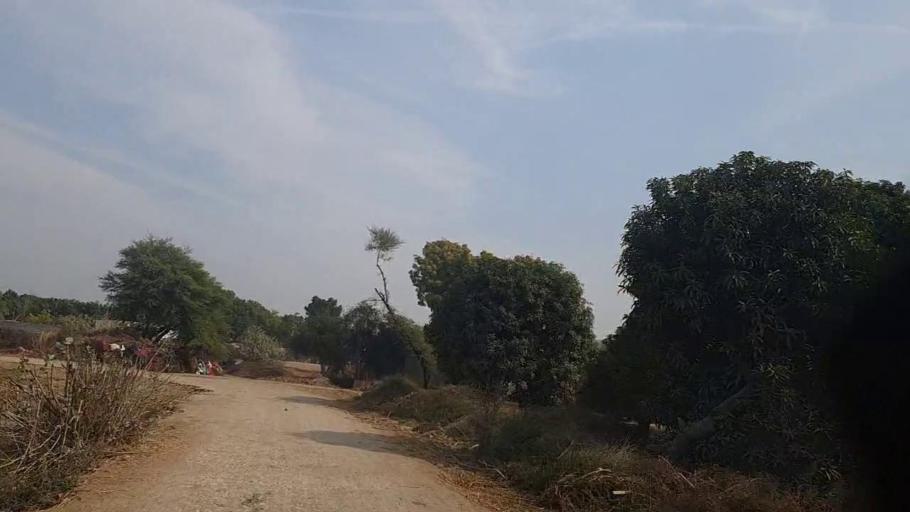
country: PK
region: Sindh
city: Daur
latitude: 26.3667
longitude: 68.2328
